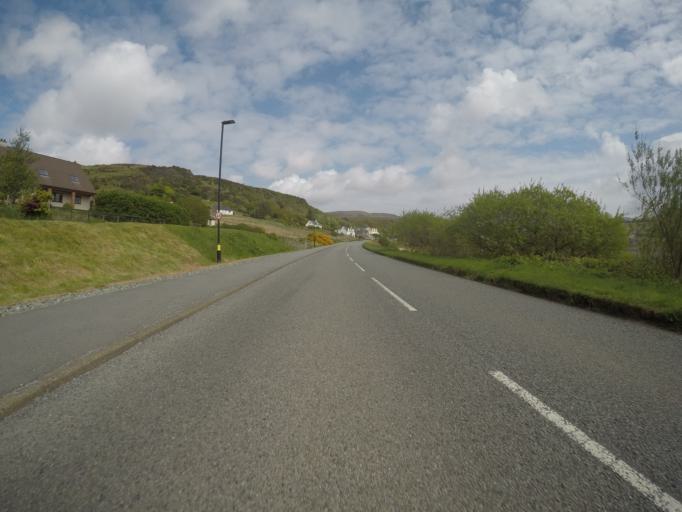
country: GB
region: Scotland
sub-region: Highland
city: Portree
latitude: 57.5903
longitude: -6.3714
